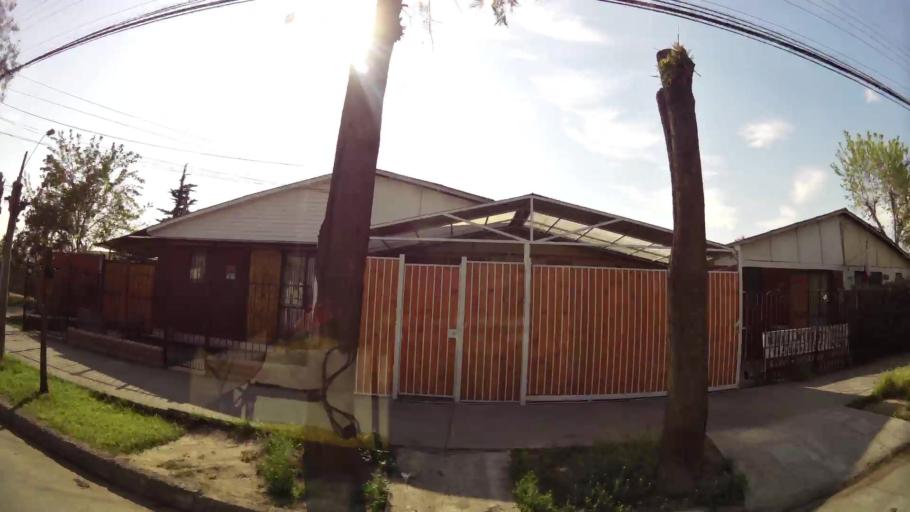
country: CL
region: Santiago Metropolitan
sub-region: Provincia de Santiago
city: La Pintana
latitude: -33.5578
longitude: -70.5979
